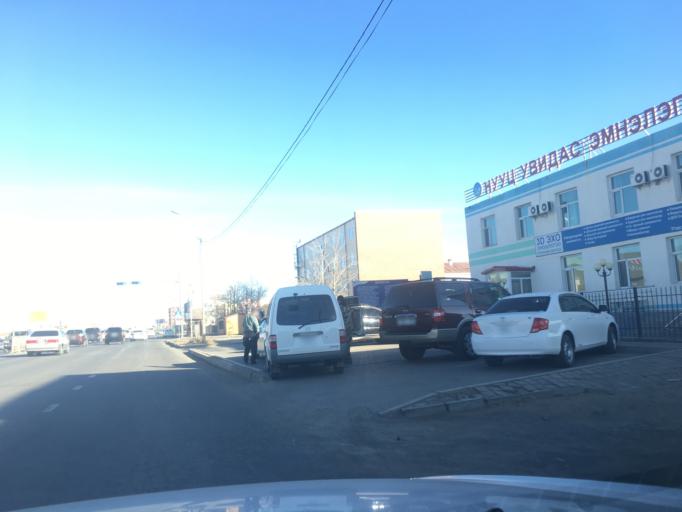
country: MN
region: Ulaanbaatar
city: Ulaanbaatar
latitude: 47.9078
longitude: 106.7916
